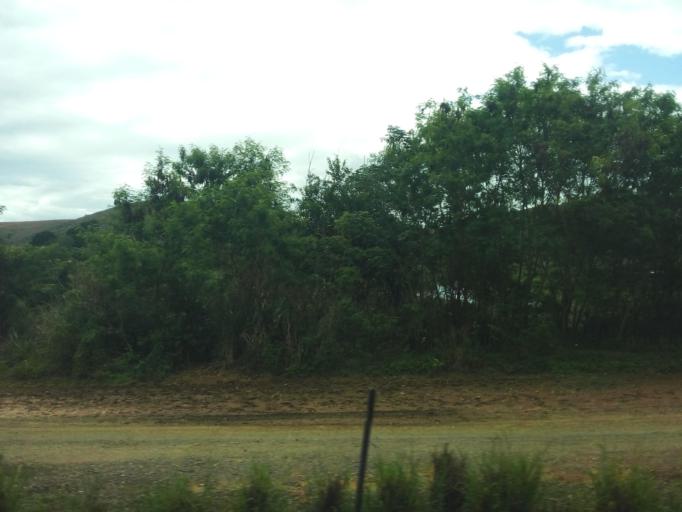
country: BR
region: Minas Gerais
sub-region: Governador Valadares
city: Governador Valadares
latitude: -19.0843
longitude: -42.1615
